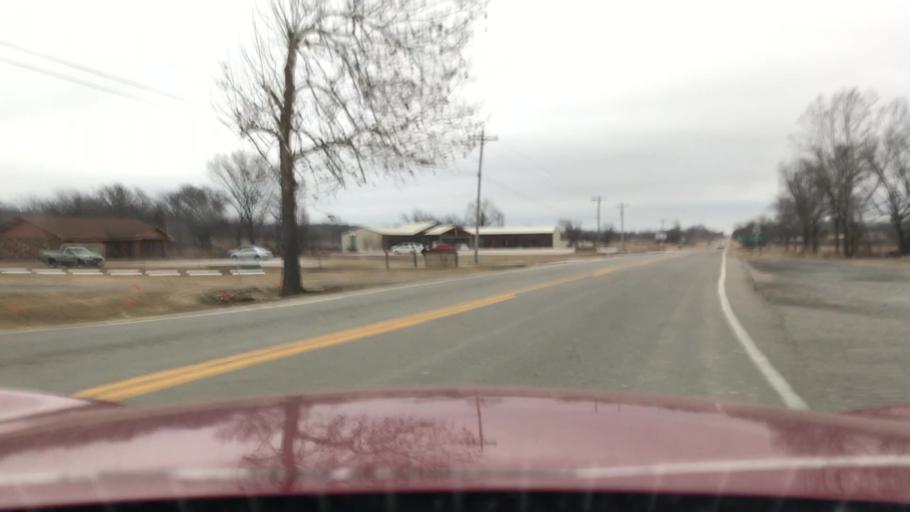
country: US
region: Oklahoma
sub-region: Sequoyah County
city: Sallisaw
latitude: 35.5070
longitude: -94.7724
